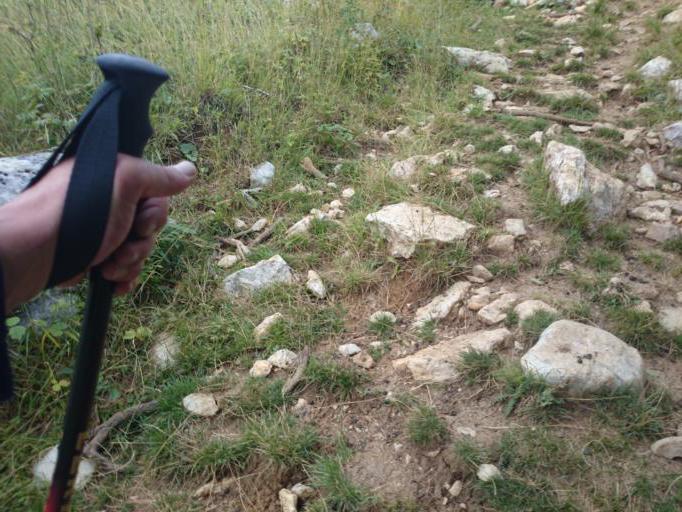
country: AL
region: Lezhe
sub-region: Rrethi i Mirdites
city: Orosh
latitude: 41.8510
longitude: 20.1560
